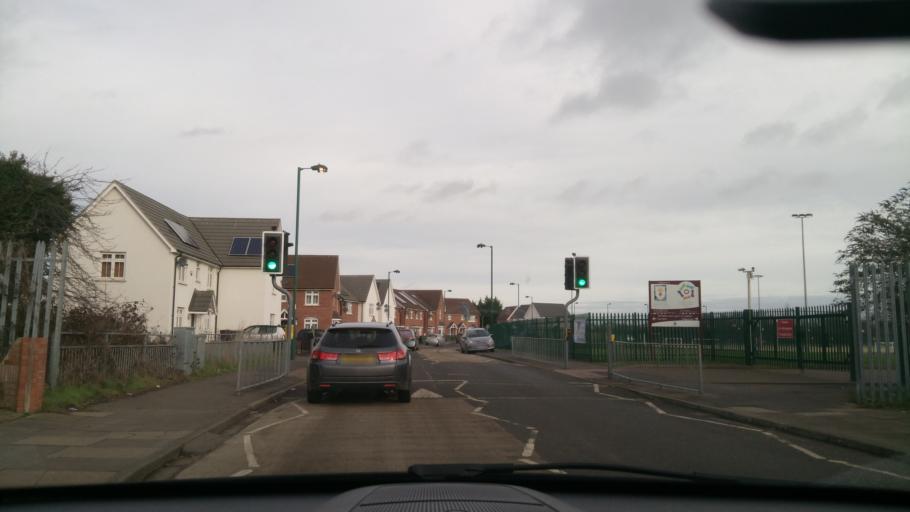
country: GB
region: England
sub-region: Peterborough
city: Peterborough
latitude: 52.5820
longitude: -0.2236
